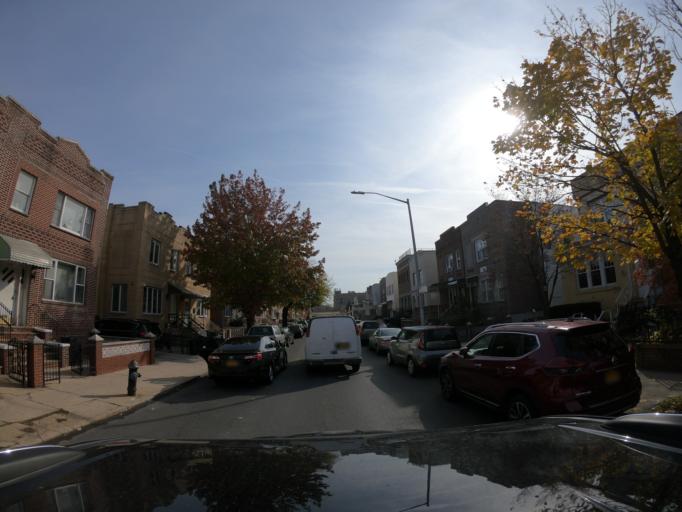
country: US
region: New York
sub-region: Kings County
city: Bensonhurst
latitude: 40.6168
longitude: -73.9816
